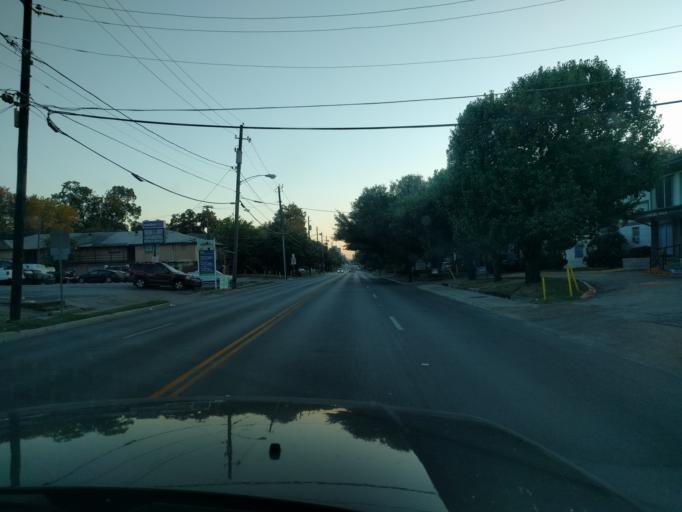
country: US
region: Texas
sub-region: Dallas County
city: Highland Park
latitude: 32.7997
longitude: -96.7699
